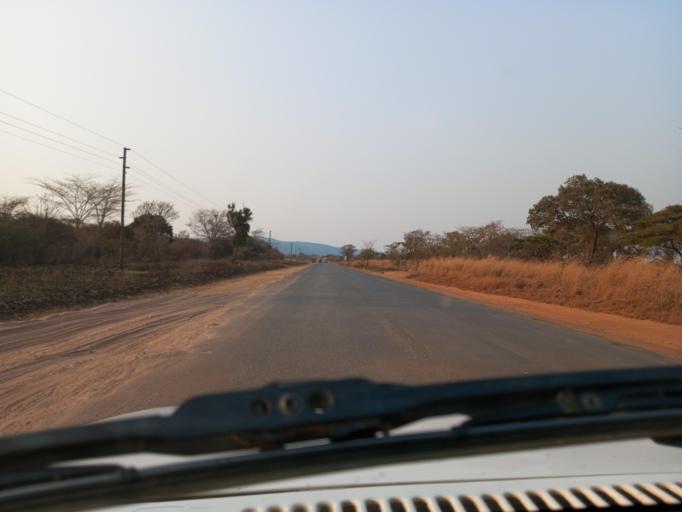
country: ZM
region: Northern
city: Mpika
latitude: -11.9234
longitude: 31.4172
